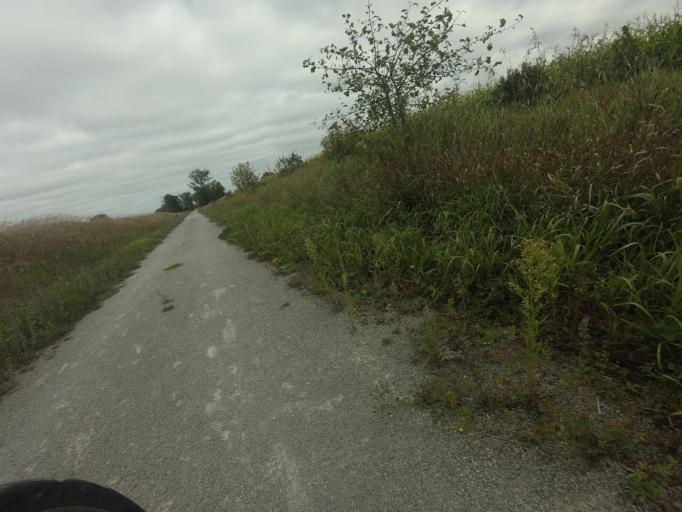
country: CA
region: Ontario
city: Omemee
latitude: 44.3137
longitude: -78.8662
